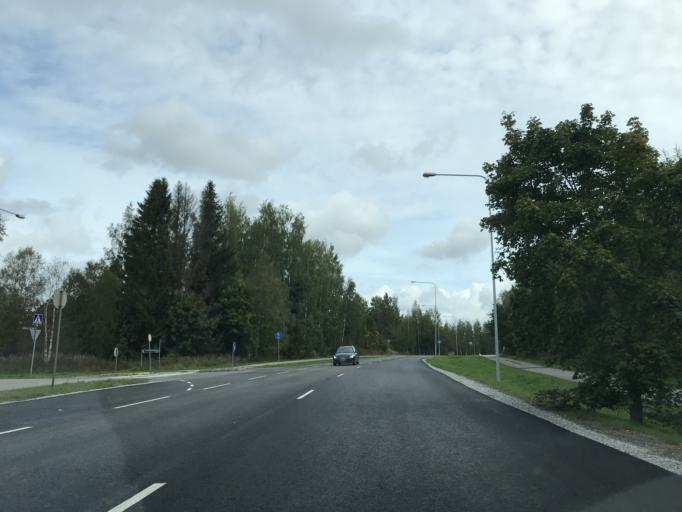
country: FI
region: Paijanne Tavastia
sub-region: Lahti
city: Lahti
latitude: 61.0090
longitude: 25.7801
